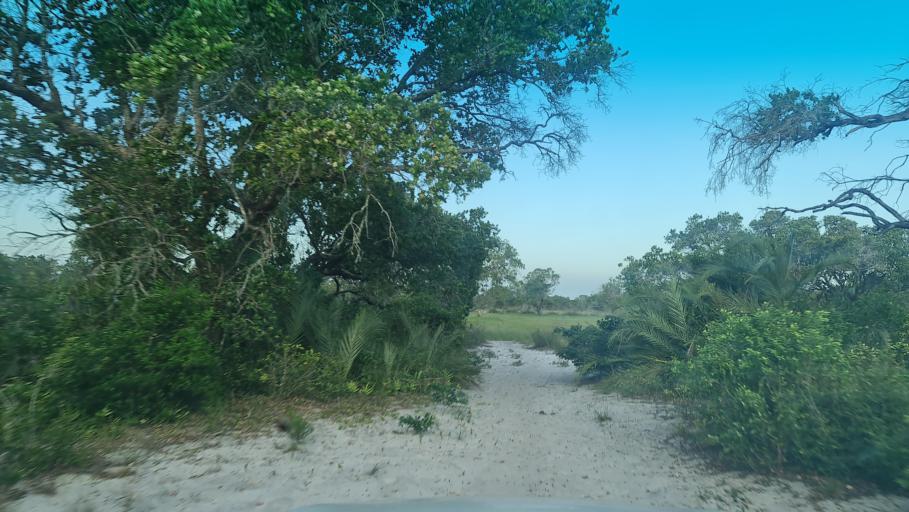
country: MZ
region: Gaza
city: Macia
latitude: -25.2165
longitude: 33.0490
